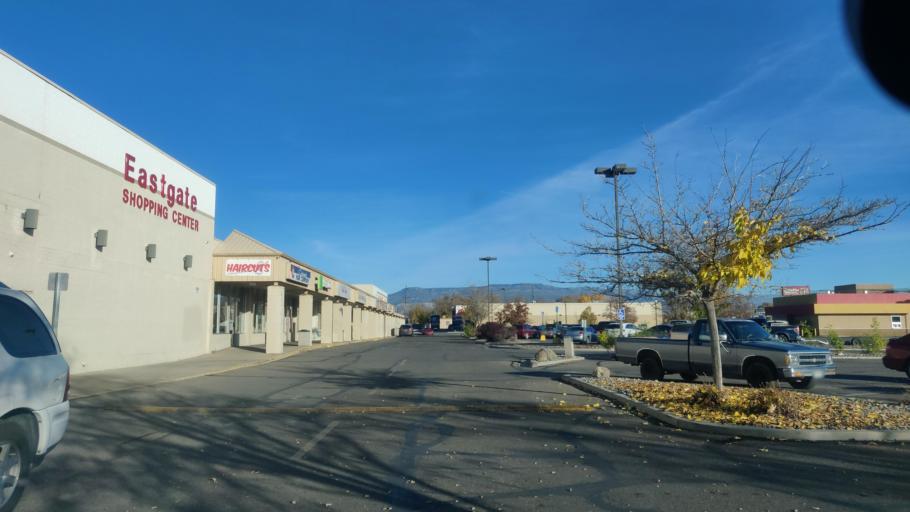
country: US
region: Colorado
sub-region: Mesa County
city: Grand Junction
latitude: 39.0783
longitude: -108.5273
